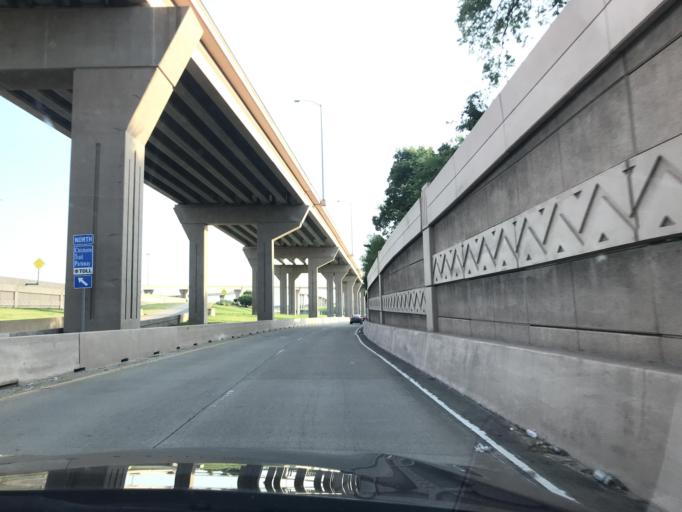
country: US
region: Texas
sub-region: Tarrant County
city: Benbrook
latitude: 32.6786
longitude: -97.4057
